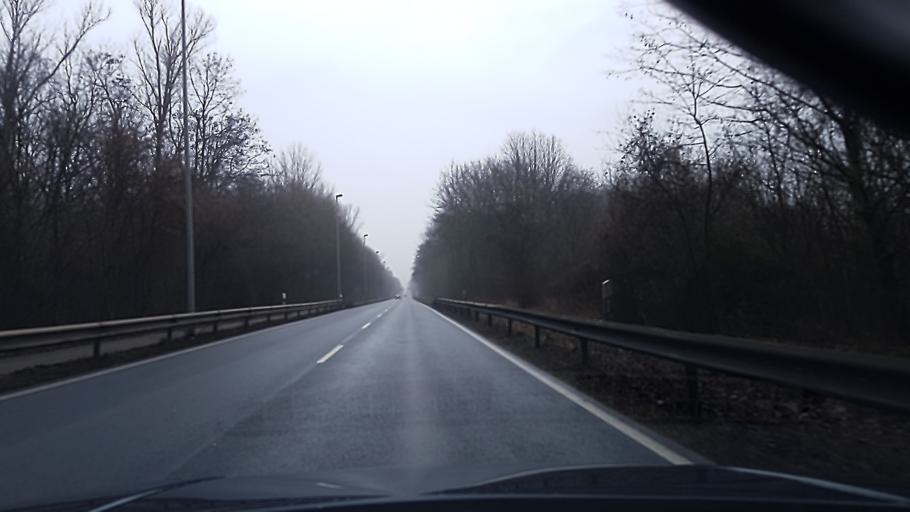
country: DE
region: Lower Saxony
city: Cramme
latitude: 52.1578
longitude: 10.4258
